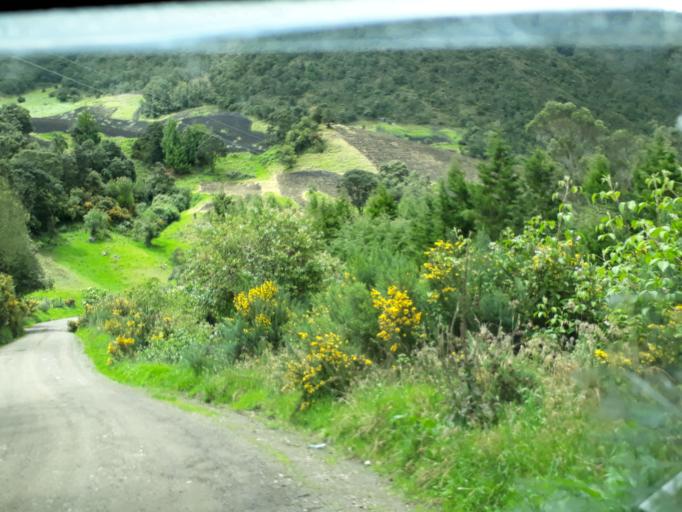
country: CO
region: Cundinamarca
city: Cogua
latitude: 5.1648
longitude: -73.9976
